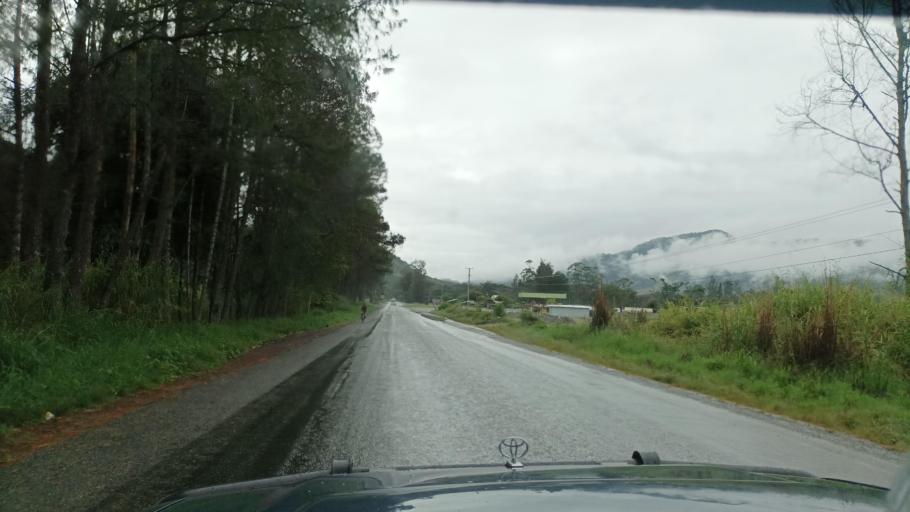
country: PG
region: Western Highlands
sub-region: Hagen
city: Mount Hagen
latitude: -5.8353
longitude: 144.3383
